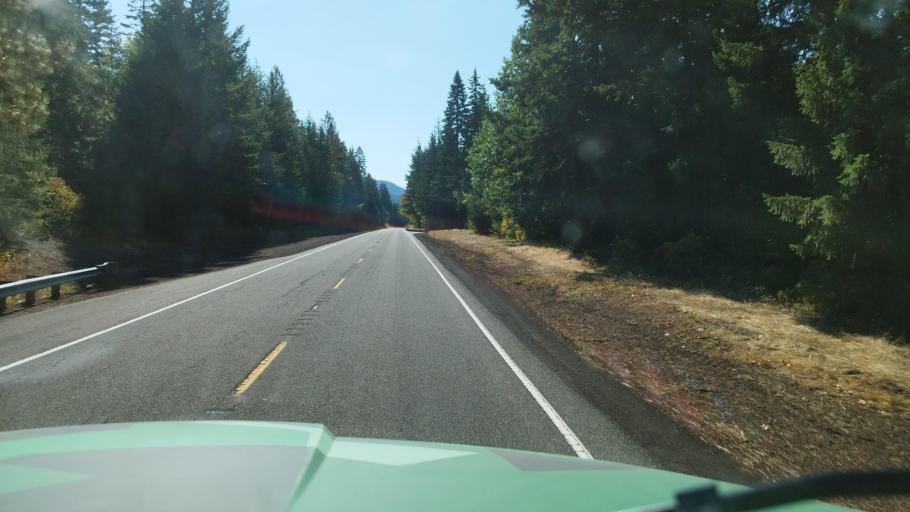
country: US
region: Oregon
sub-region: Hood River County
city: Odell
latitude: 45.5150
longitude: -121.5648
